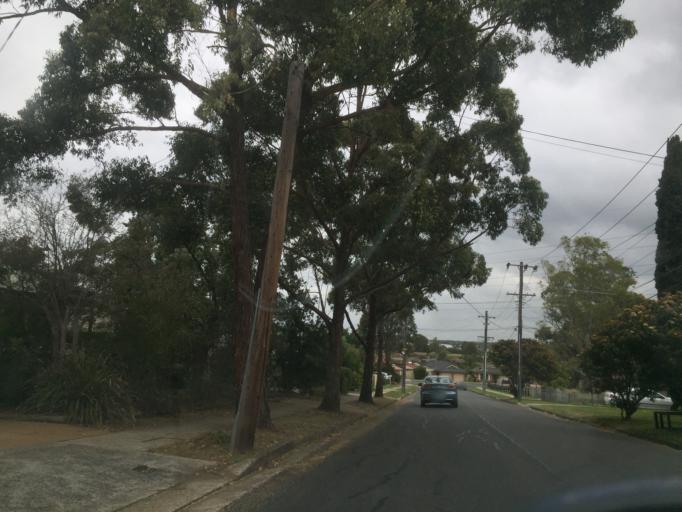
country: AU
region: New South Wales
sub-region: Blacktown
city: Doonside
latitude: -33.7808
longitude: 150.8901
